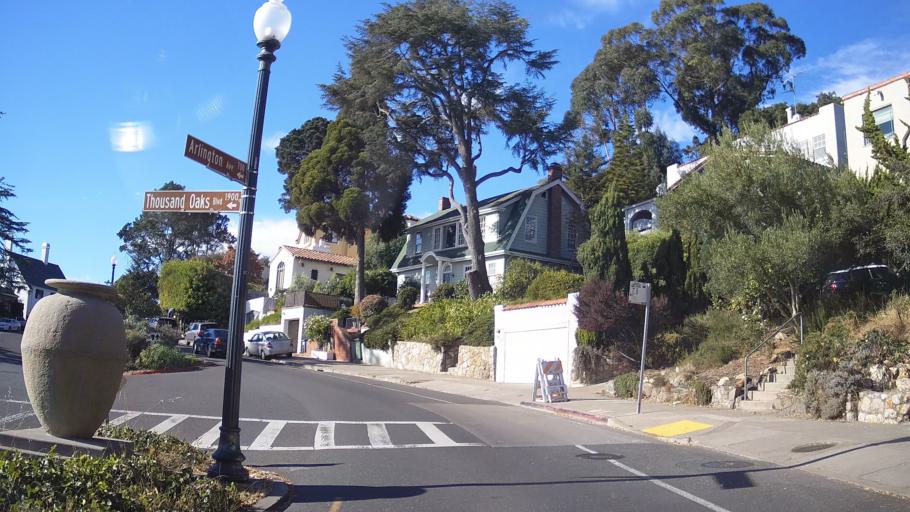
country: US
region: California
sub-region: Contra Costa County
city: Kensington
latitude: 37.8972
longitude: -122.2758
